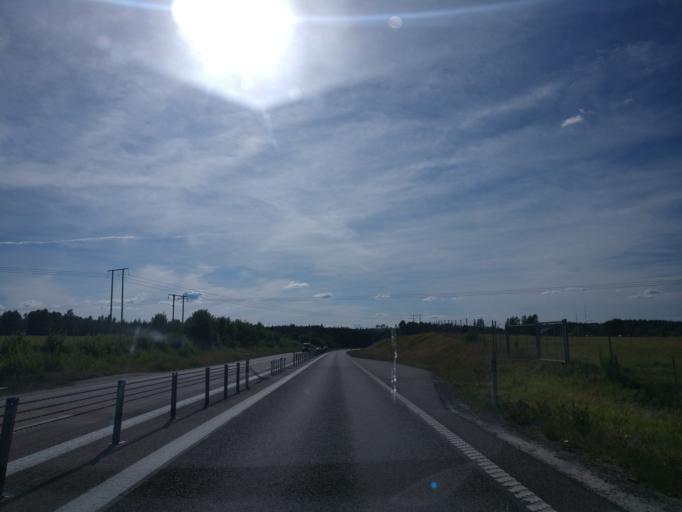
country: SE
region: Vaermland
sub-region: Kils Kommun
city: Kil
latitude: 59.5097
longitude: 13.2310
